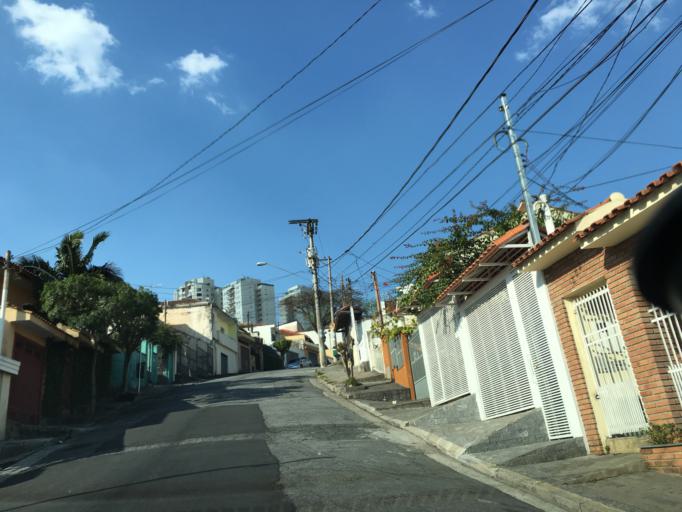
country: BR
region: Sao Paulo
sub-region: Sao Paulo
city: Sao Paulo
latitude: -23.4731
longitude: -46.6336
